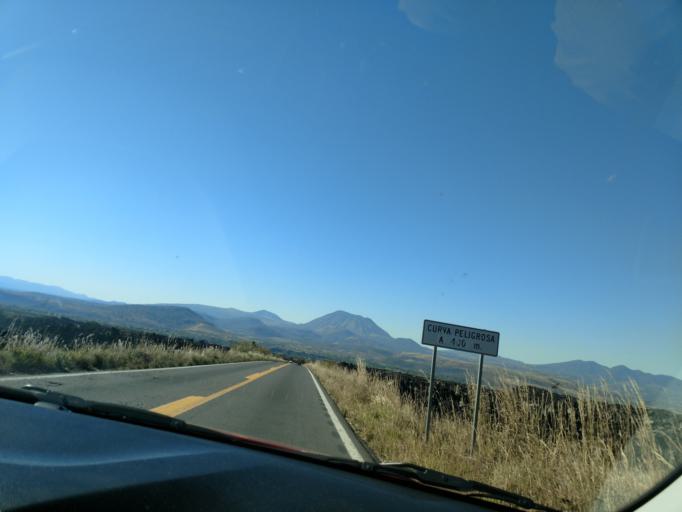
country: MX
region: Nayarit
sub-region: Ahuacatlan
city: Ahuacatlan
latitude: 21.0936
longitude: -104.5780
